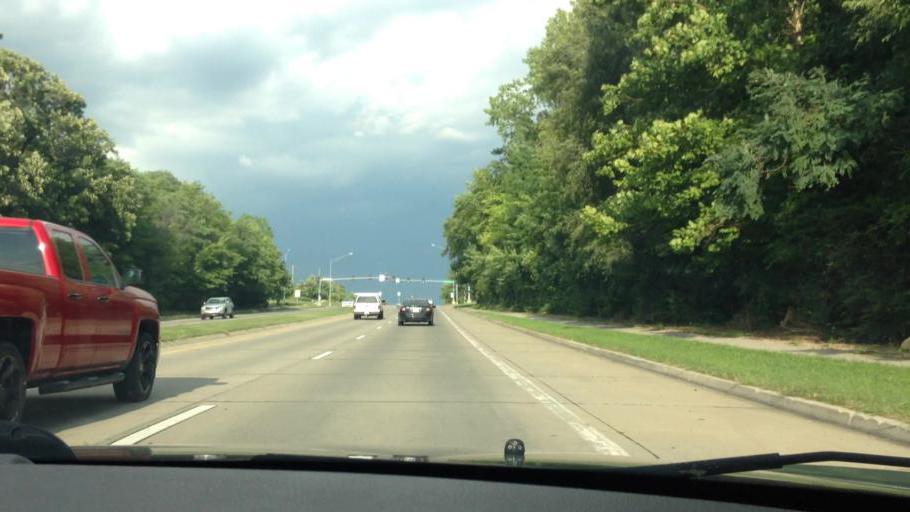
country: US
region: Missouri
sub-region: Platte County
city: Parkville
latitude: 39.2105
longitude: -94.6667
